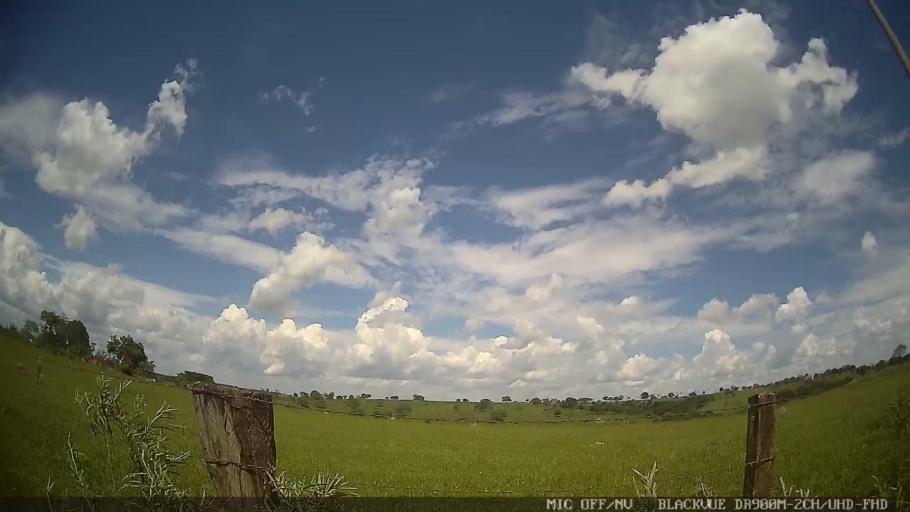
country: BR
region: Sao Paulo
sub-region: Conchas
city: Conchas
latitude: -23.0366
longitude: -47.9956
